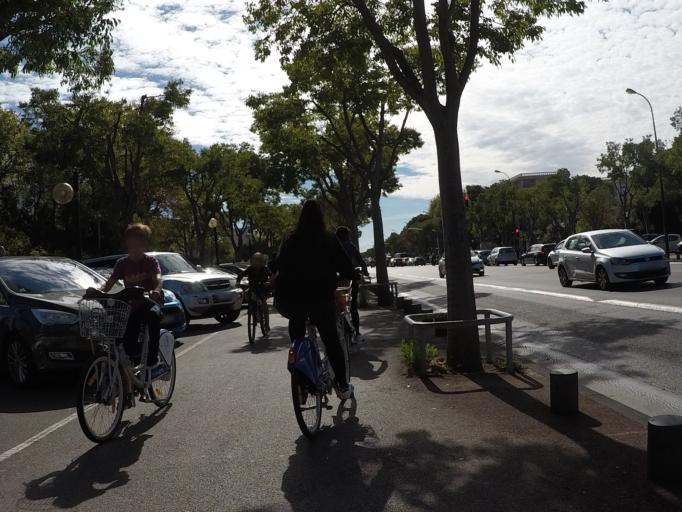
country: FR
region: Provence-Alpes-Cote d'Azur
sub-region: Departement des Bouches-du-Rhone
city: Marseille 08
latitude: 43.2648
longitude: 5.3793
